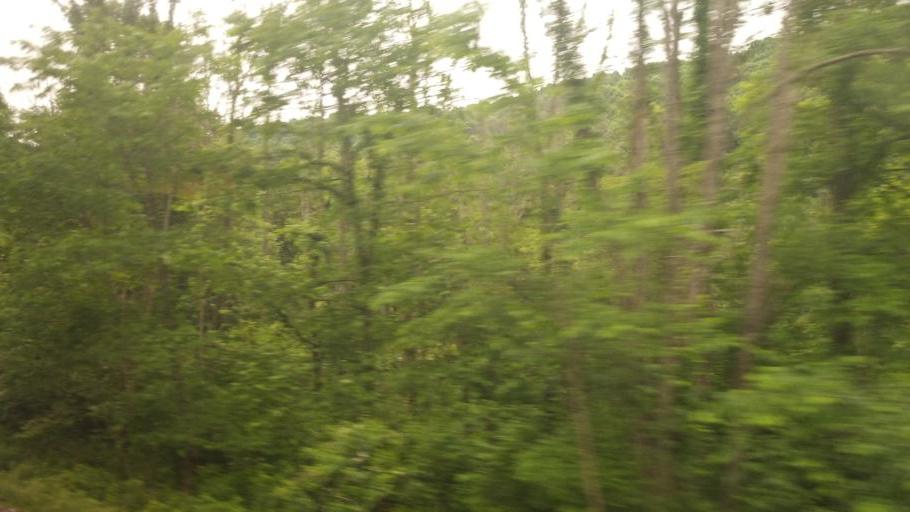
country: US
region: Pennsylvania
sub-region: Somerset County
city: Milford
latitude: 39.8479
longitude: -79.2339
